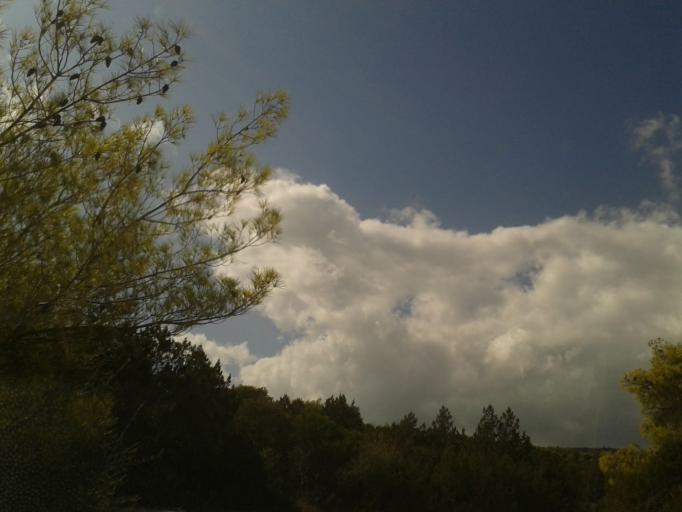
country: GR
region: Attica
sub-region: Nomarchia Anatolikis Attikis
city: Kato Soulion
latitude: 38.2257
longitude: 24.0250
